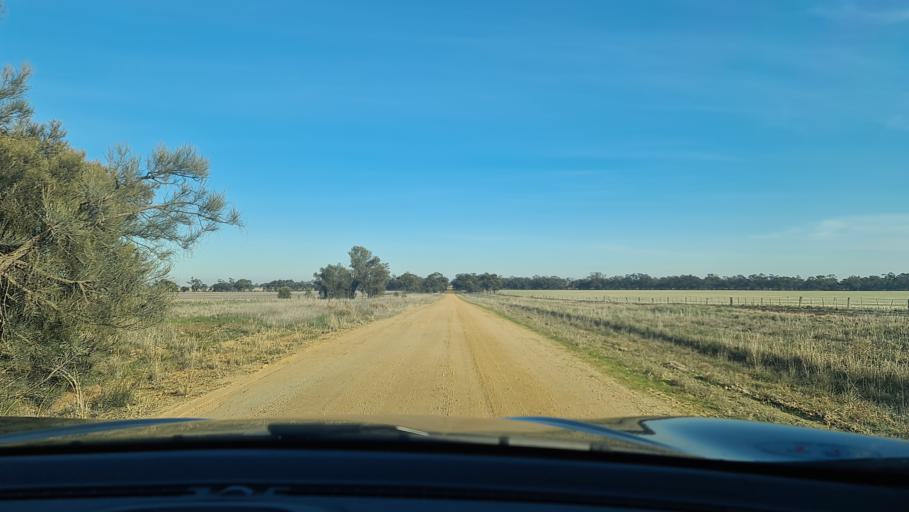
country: AU
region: Victoria
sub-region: Horsham
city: Horsham
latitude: -36.3538
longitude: 142.4050
